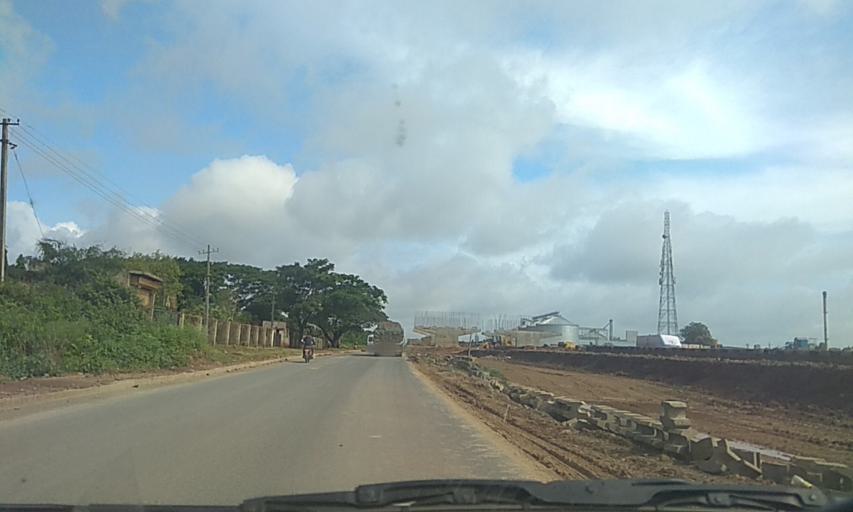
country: IN
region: Karnataka
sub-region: Haveri
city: Shiggaon
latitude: 15.0384
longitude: 75.1725
